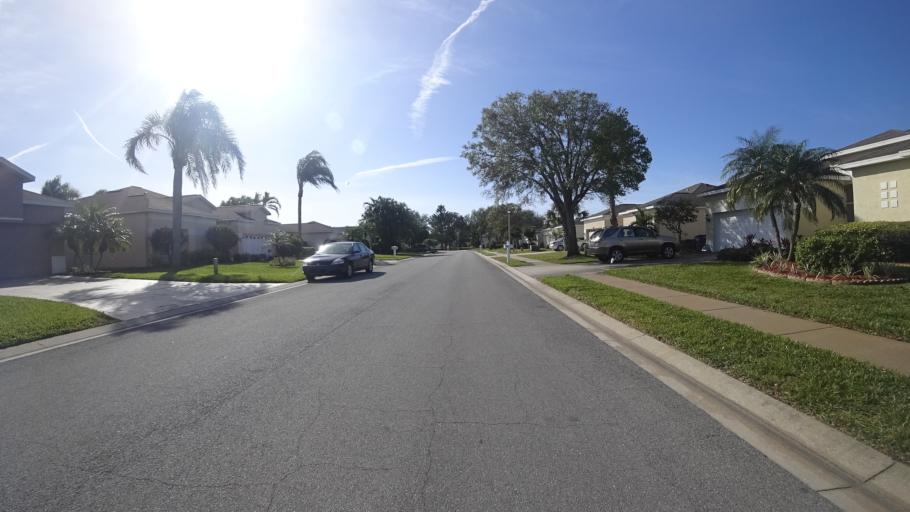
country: US
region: Florida
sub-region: Manatee County
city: South Bradenton
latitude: 27.4516
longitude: -82.6078
